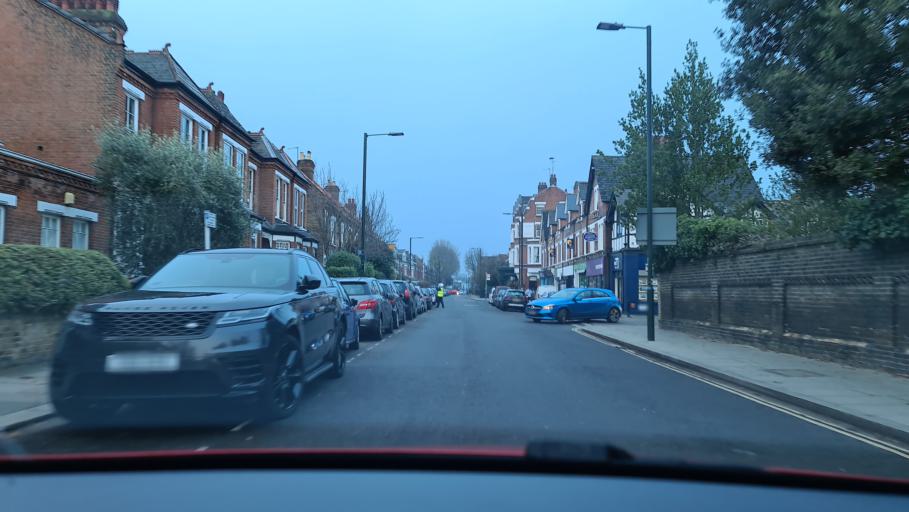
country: GB
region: England
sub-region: Greater London
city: Richmond
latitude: 51.4771
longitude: -0.2867
